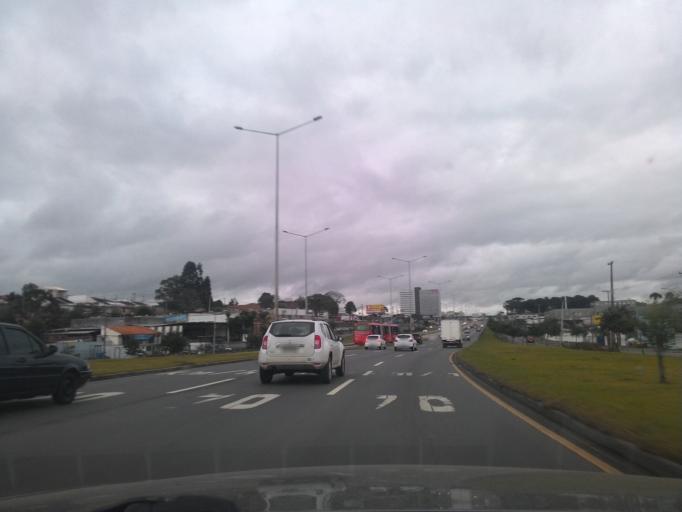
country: BR
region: Parana
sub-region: Curitiba
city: Curitiba
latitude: -25.5051
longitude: -49.2827
